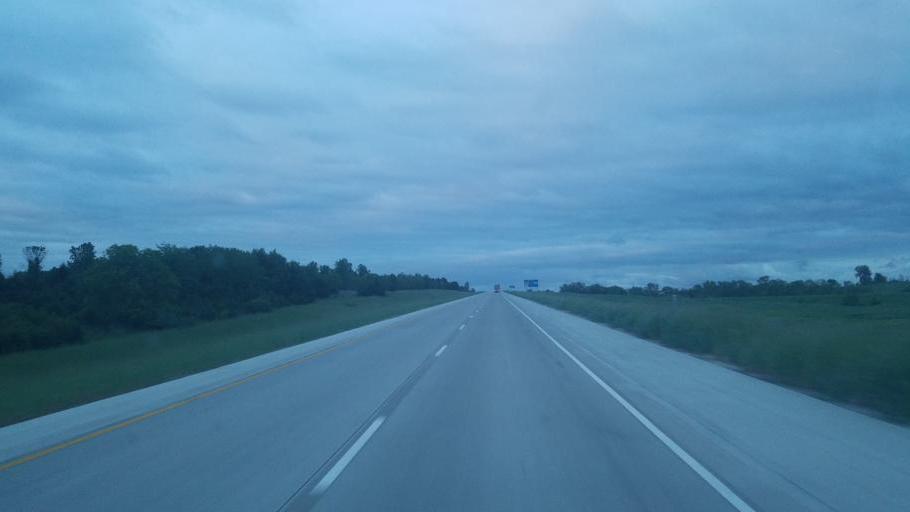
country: US
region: Iowa
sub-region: Decatur County
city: Lamoni
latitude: 40.6115
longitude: -93.8992
